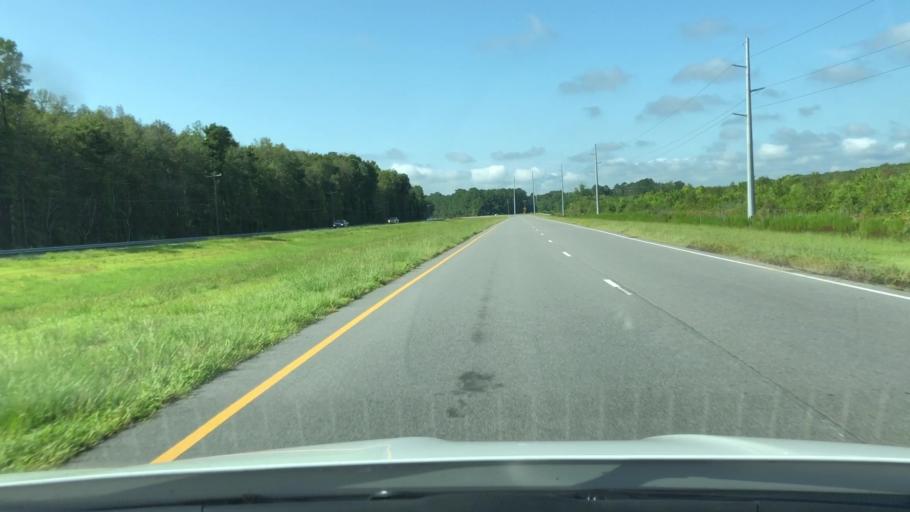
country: US
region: North Carolina
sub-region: Pasquotank County
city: Elizabeth City
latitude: 36.4324
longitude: -76.3398
